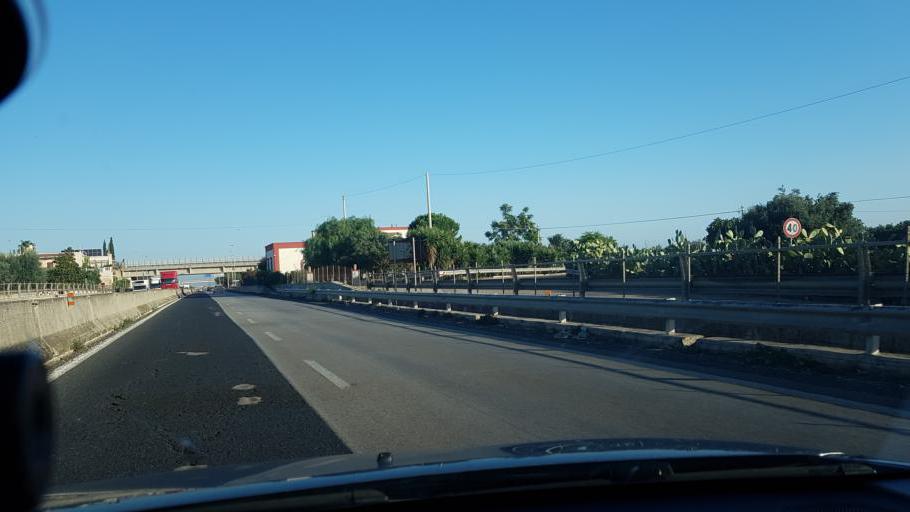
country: IT
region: Apulia
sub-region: Provincia di Brindisi
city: Fasano
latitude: 40.8784
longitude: 17.3394
